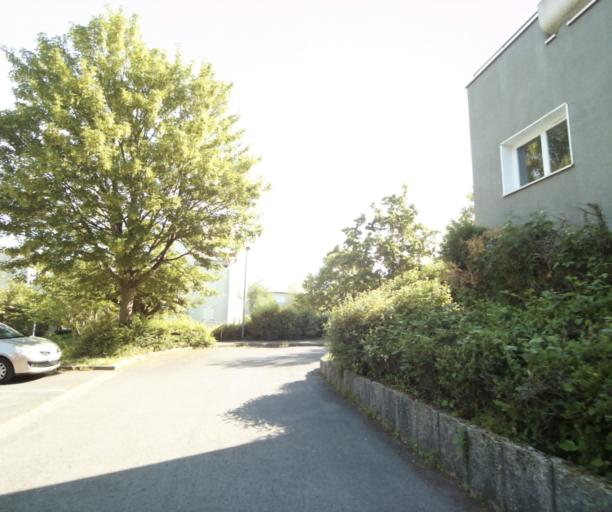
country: FR
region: Champagne-Ardenne
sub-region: Departement des Ardennes
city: La Francheville
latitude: 49.7404
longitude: 4.7184
